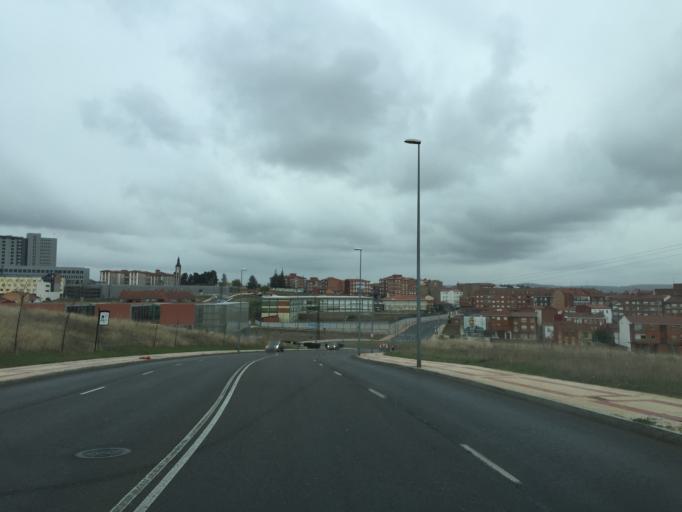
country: ES
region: Castille and Leon
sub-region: Provincia de Leon
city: Leon
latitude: 42.6132
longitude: -5.5742
